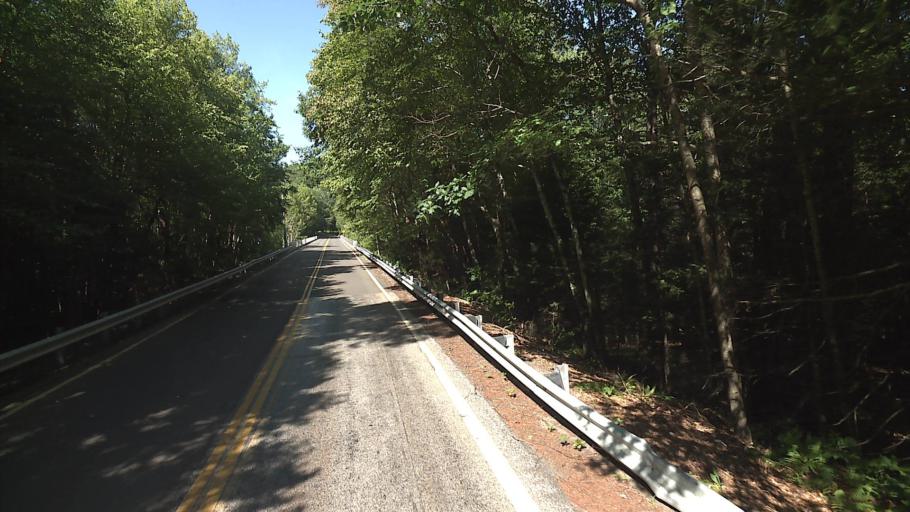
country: US
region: Connecticut
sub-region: Litchfield County
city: Plymouth
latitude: 41.7096
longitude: -73.0572
